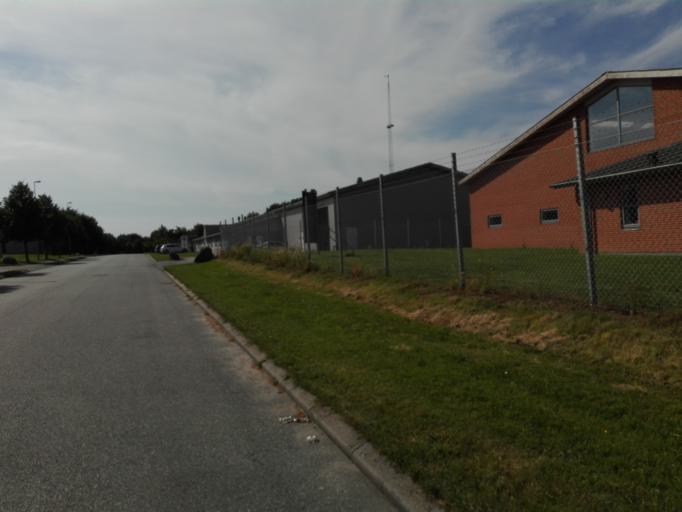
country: DK
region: Central Jutland
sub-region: Arhus Kommune
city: Tranbjerg
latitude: 56.1035
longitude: 10.1217
